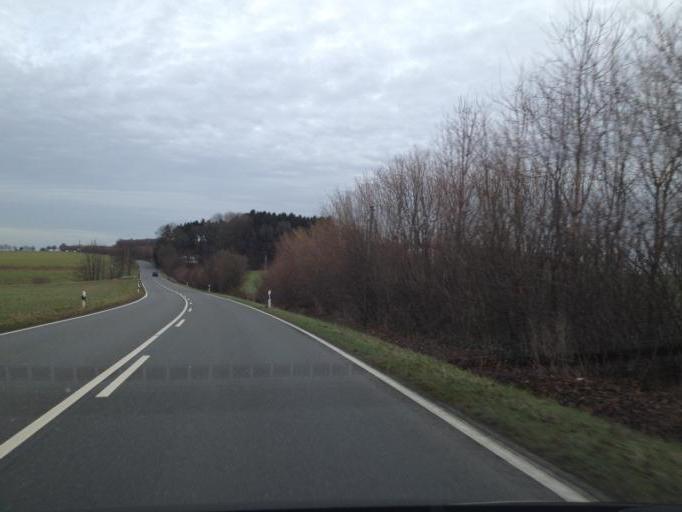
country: DE
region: North Rhine-Westphalia
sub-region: Regierungsbezirk Arnsberg
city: Soest
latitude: 51.5028
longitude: 8.0199
